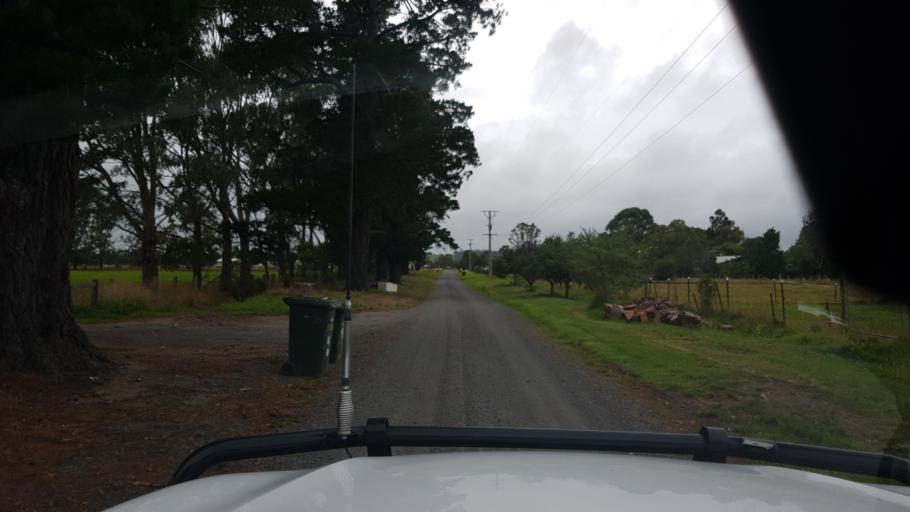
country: AU
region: Victoria
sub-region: Cardinia
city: Bunyip
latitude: -38.0941
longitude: 145.7697
